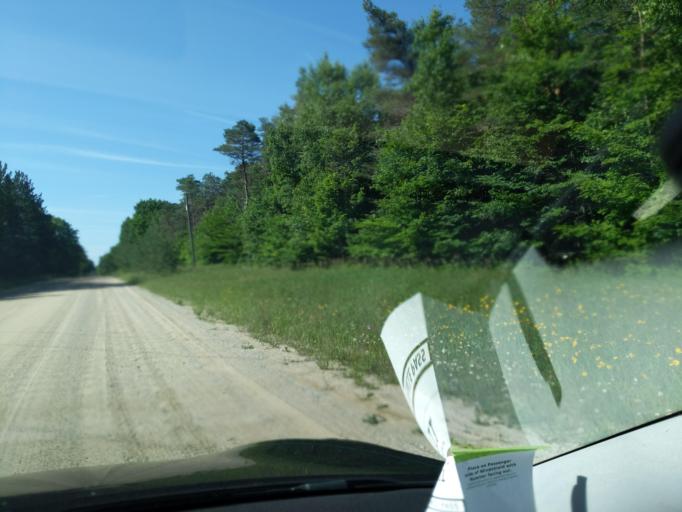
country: US
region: Michigan
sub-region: Cheboygan County
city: Cheboygan
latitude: 45.6772
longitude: -84.6507
